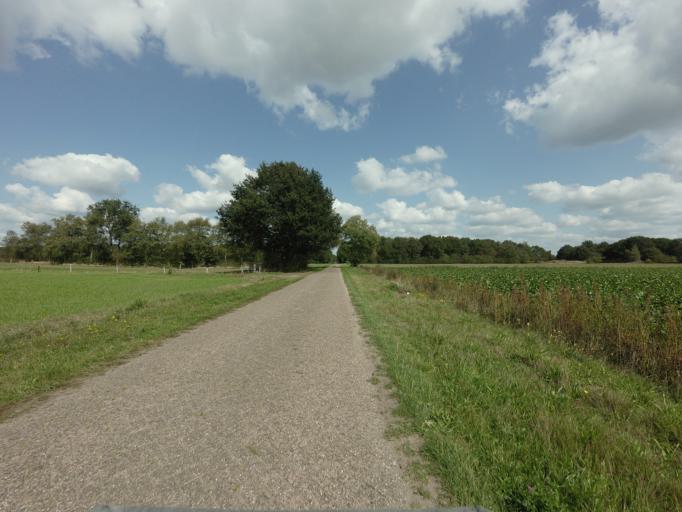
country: NL
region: Drenthe
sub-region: Gemeente Westerveld
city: Dwingeloo
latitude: 52.8768
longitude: 6.3818
